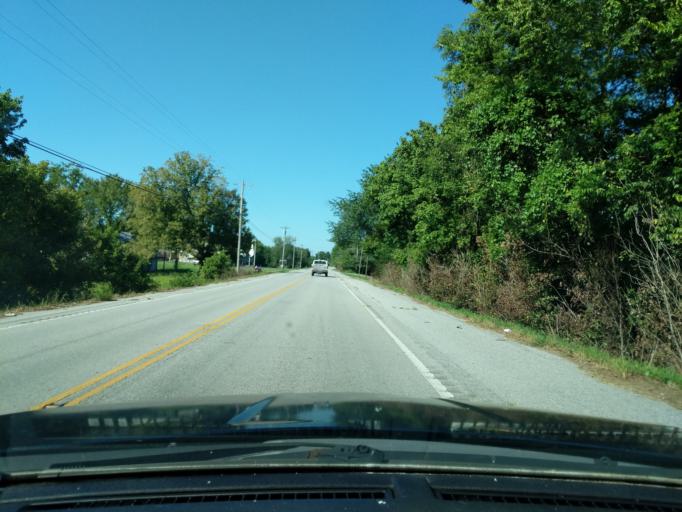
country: US
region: Tennessee
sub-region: Smith County
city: Carthage
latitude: 36.2618
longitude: -86.0725
